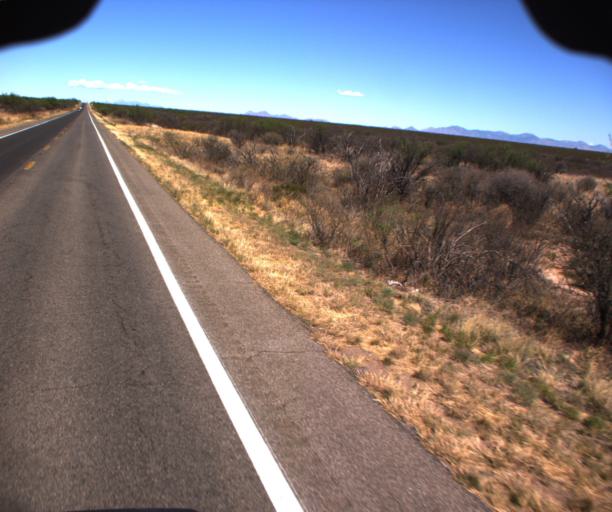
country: US
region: Arizona
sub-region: Cochise County
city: Sierra Vista Southeast
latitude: 31.5486
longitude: -110.1717
